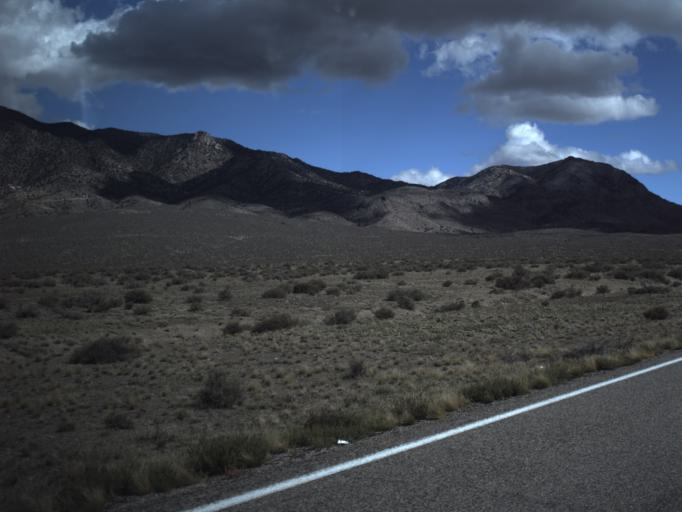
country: US
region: Utah
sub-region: Beaver County
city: Milford
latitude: 38.4462
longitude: -113.3326
